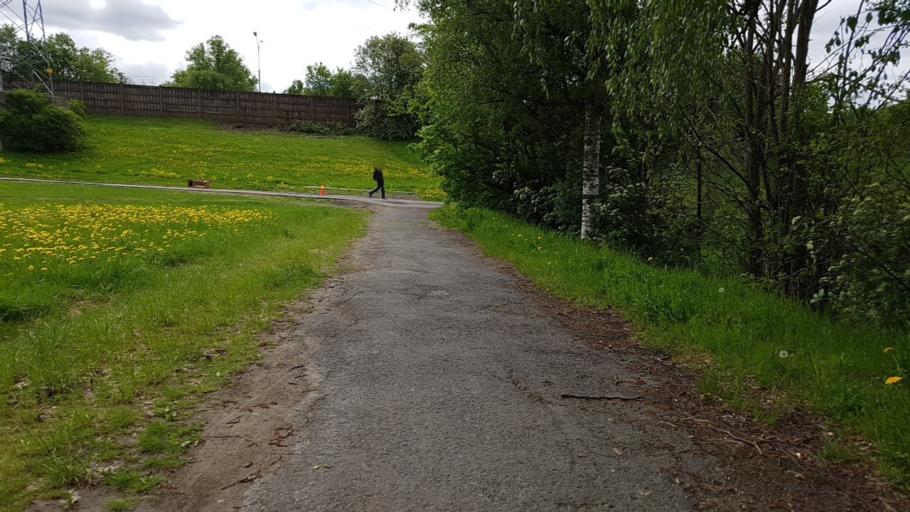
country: NO
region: Oslo
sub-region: Oslo
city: Oslo
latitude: 59.9418
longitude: 10.7993
